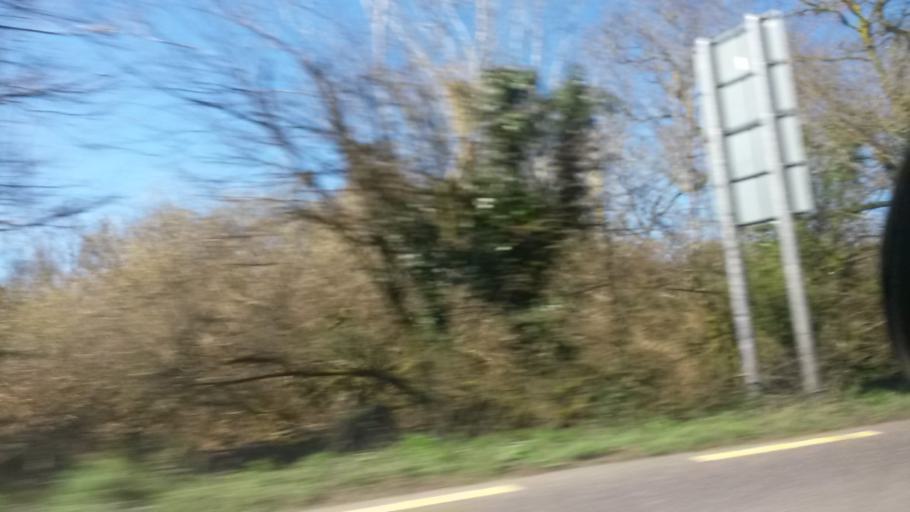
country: IE
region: Munster
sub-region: County Cork
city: Millstreet
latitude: 51.9475
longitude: -9.1777
